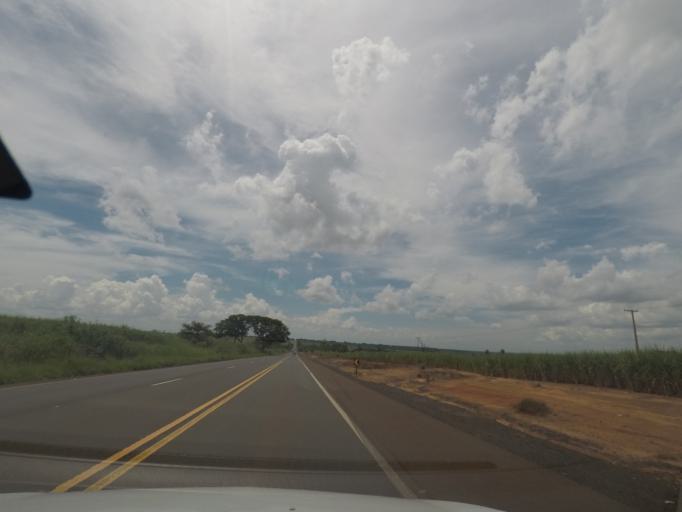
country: BR
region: Sao Paulo
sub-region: Barretos
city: Barretos
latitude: -20.3782
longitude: -48.6433
